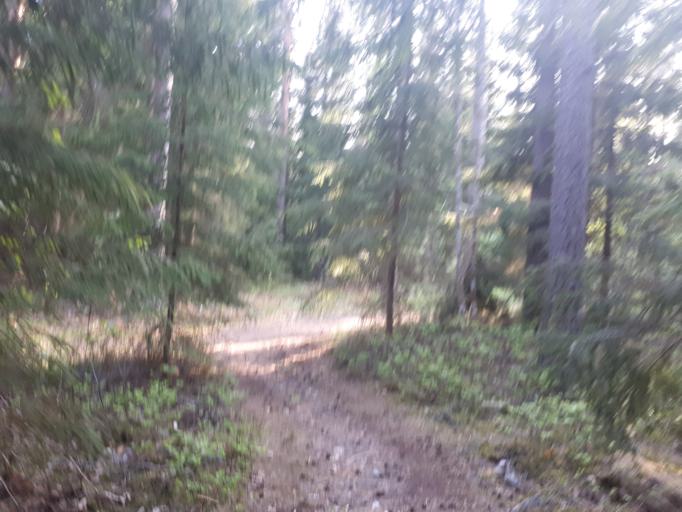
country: SE
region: Soedermanland
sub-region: Flens Kommun
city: Halleforsnas
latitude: 59.0643
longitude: 16.4026
